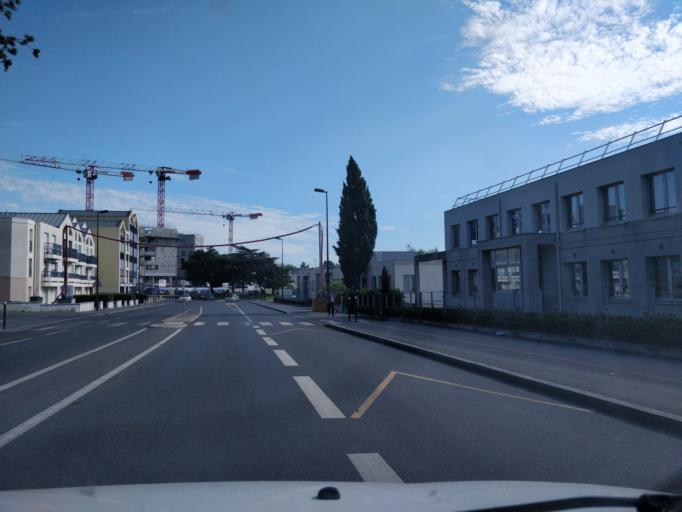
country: FR
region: Pays de la Loire
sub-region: Departement de la Loire-Atlantique
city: Nantes
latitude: 47.2440
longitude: -1.5338
